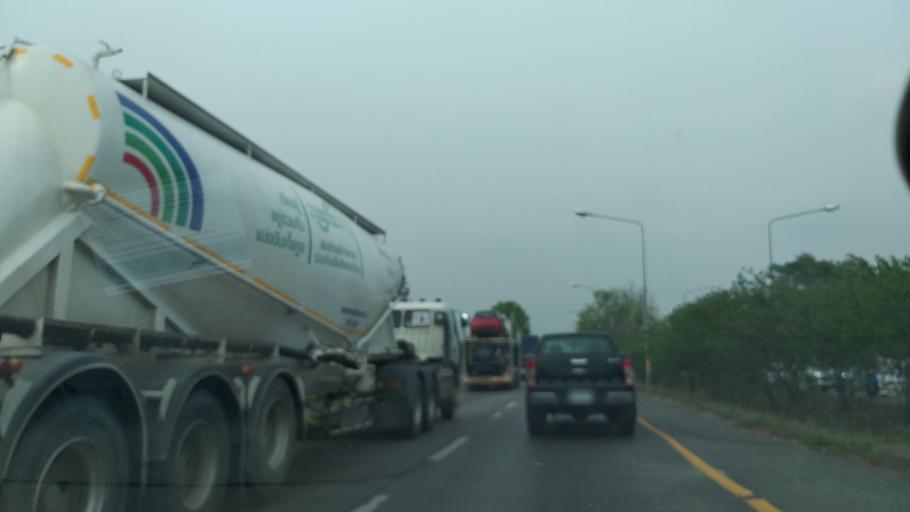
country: TH
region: Chon Buri
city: Ban Bueng
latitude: 13.2840
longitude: 101.2561
